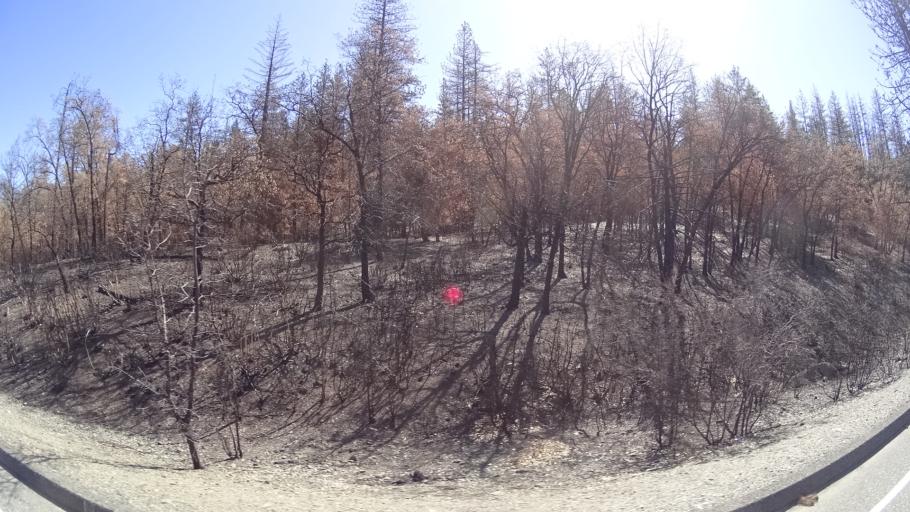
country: US
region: California
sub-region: Tehama County
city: Rancho Tehama Reserve
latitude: 39.6784
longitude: -122.7110
